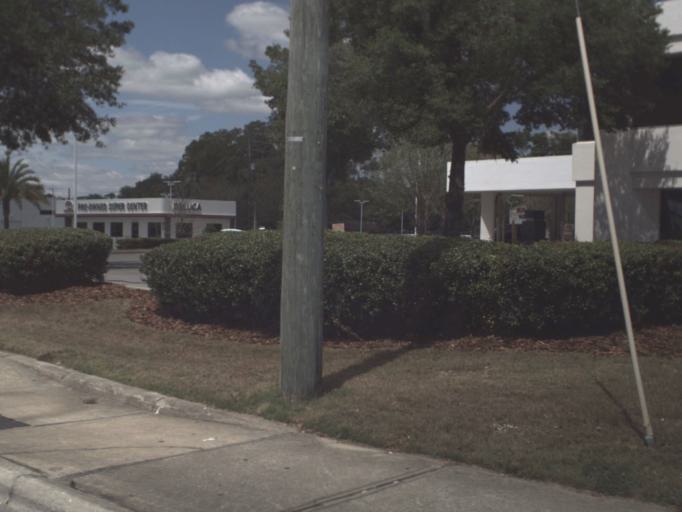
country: US
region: Florida
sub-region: Marion County
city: Ocala
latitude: 29.1787
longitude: -82.1527
